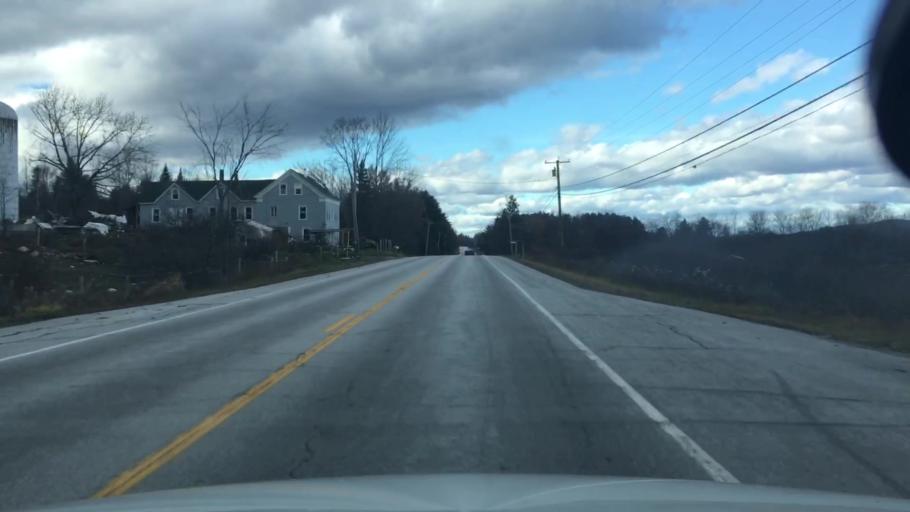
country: US
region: Maine
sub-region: Somerset County
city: Palmyra
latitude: 44.8367
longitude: -69.4206
